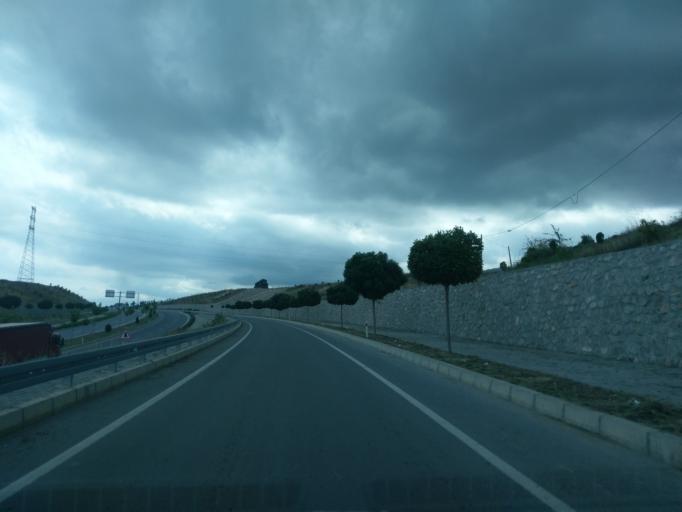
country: TR
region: Sinop
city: Gerze
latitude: 41.8111
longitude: 35.1673
